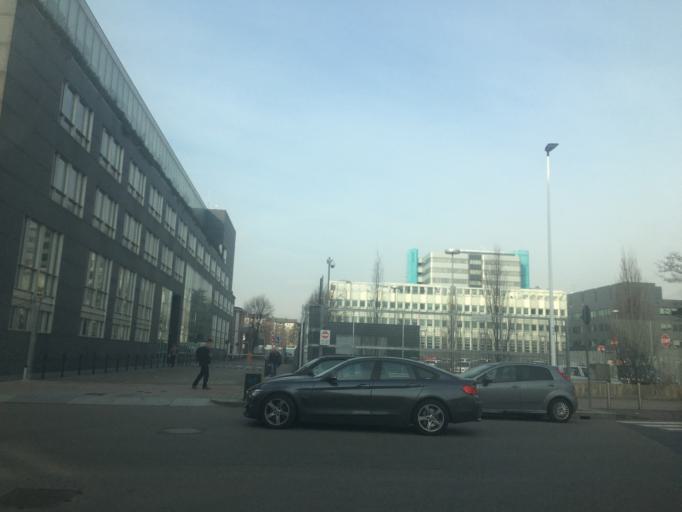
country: IT
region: Lombardy
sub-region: Citta metropolitana di Milano
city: Sesto San Giovanni
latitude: 45.5193
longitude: 9.2137
